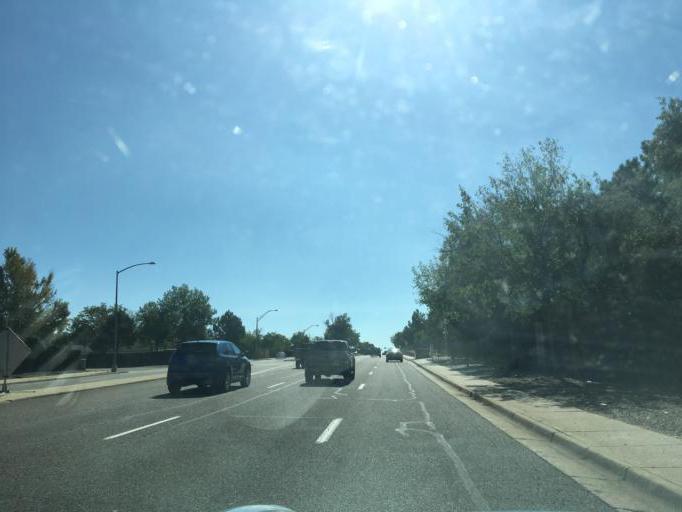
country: US
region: Colorado
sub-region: Arapahoe County
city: Dove Valley
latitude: 39.6307
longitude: -104.8049
